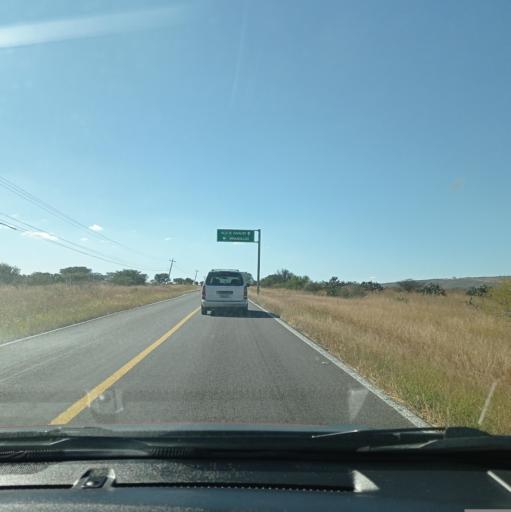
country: MX
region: Jalisco
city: San Miguel el Alto
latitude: 21.0198
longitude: -102.4556
